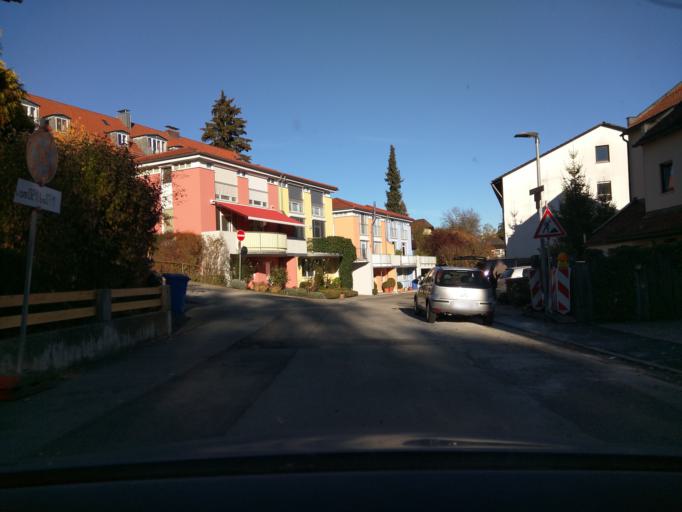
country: DE
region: Bavaria
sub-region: Lower Bavaria
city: Passau
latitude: 48.5659
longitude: 13.4394
